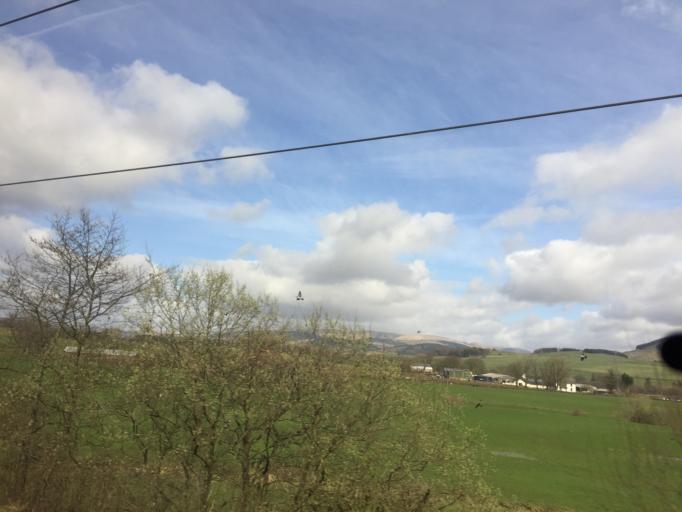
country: GB
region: Scotland
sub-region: Dumfries and Galloway
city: Moffat
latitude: 55.2883
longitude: -3.4303
